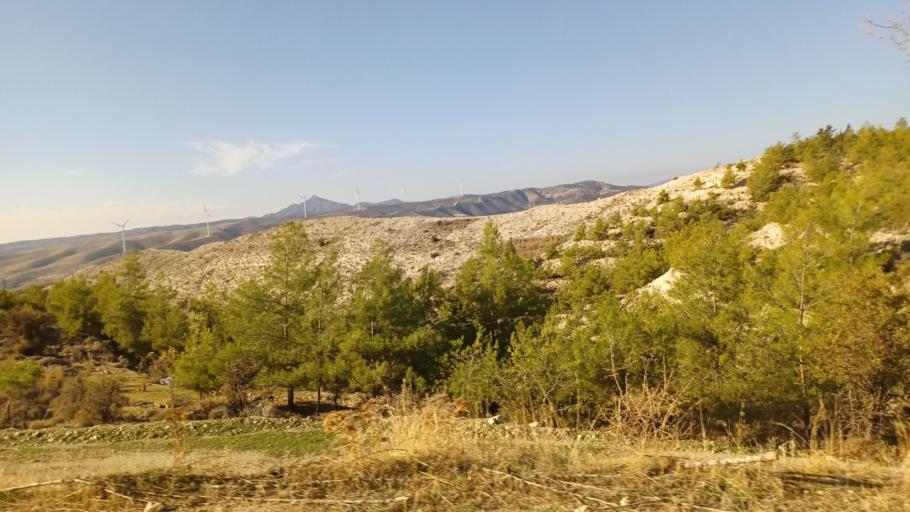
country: CY
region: Larnaka
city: Psevdas
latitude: 34.9505
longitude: 33.5109
